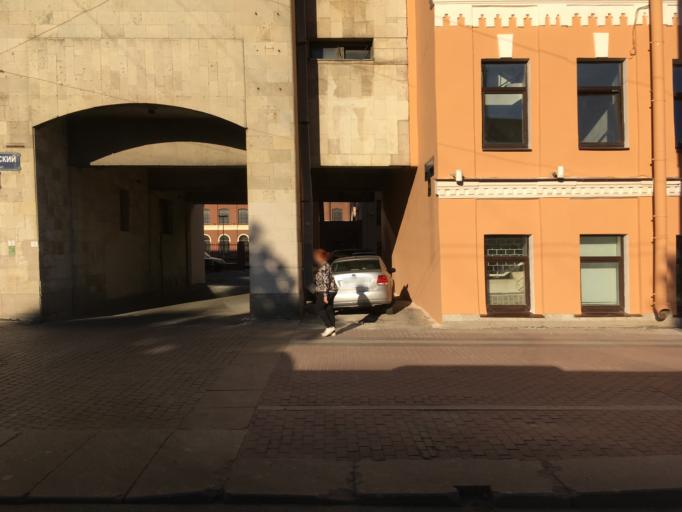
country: RU
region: St.-Petersburg
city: Admiralteisky
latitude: 59.8859
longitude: 30.3203
